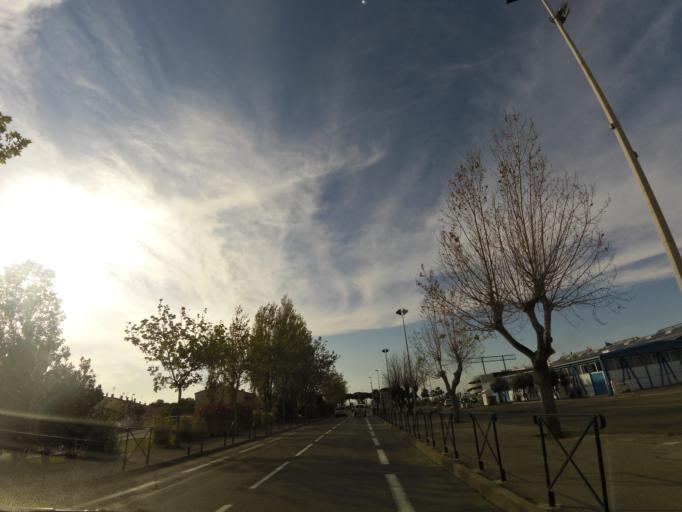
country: FR
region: Languedoc-Roussillon
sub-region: Departement de l'Herault
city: Palavas-les-Flots
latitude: 43.5312
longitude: 3.9280
